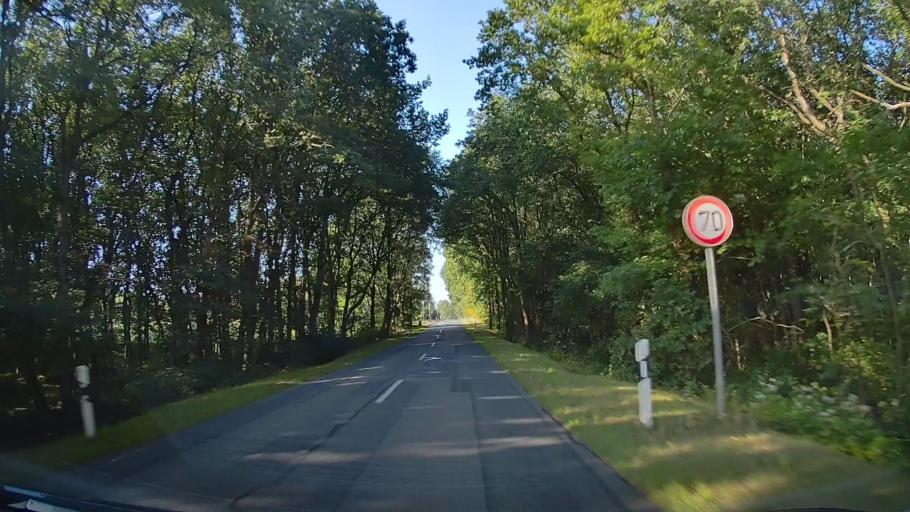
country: DE
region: Lower Saxony
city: Nordholz
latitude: 53.8122
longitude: 8.5978
